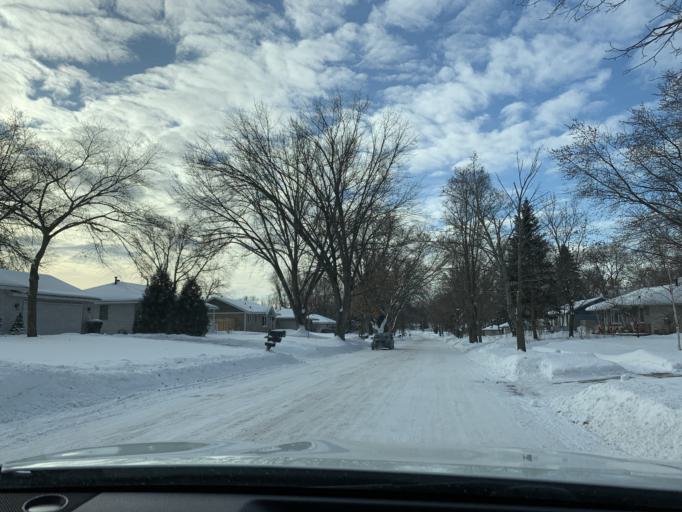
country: US
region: Minnesota
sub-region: Anoka County
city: Blaine
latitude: 45.1728
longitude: -93.2846
